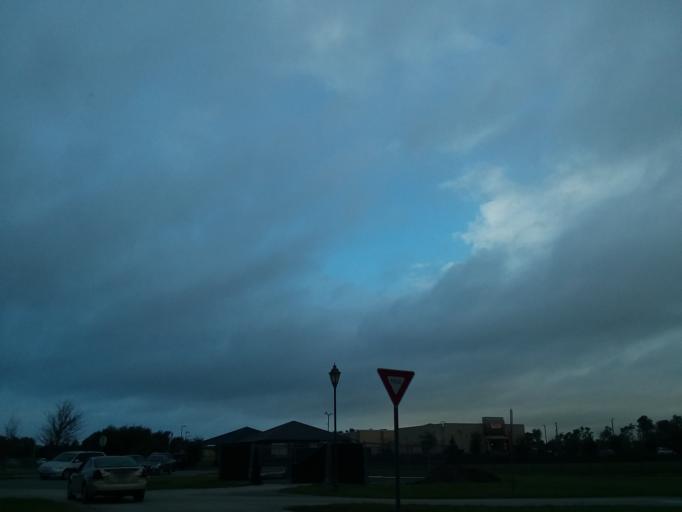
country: US
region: Florida
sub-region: Osceola County
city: Poinciana
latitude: 28.1854
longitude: -81.4374
